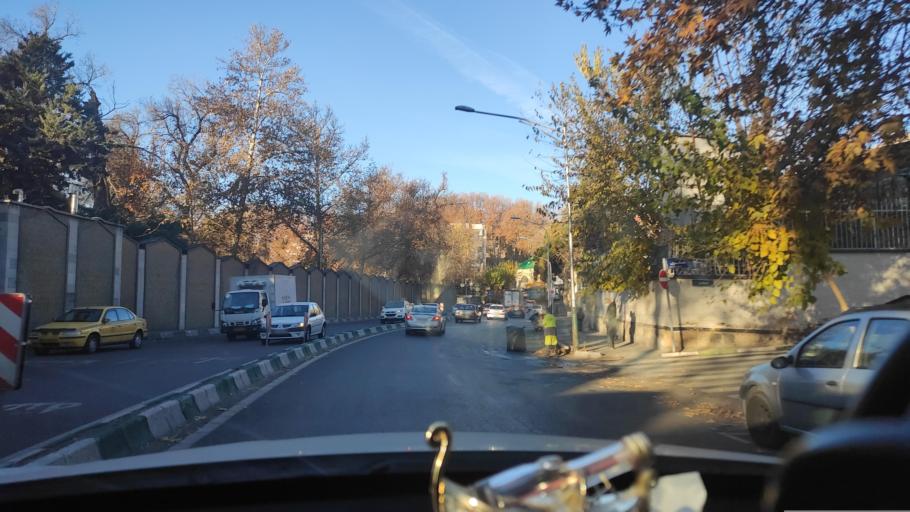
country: IR
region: Tehran
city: Tajrish
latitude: 35.8130
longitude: 51.4728
